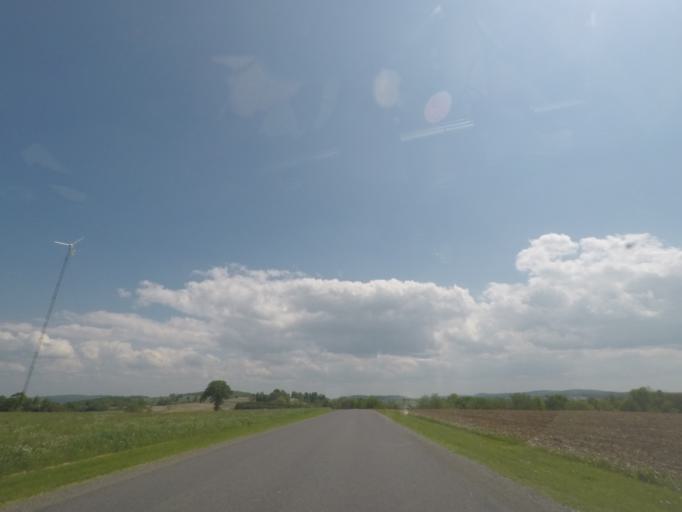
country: US
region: New York
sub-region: Dutchess County
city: Pine Plains
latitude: 41.9787
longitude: -73.5504
